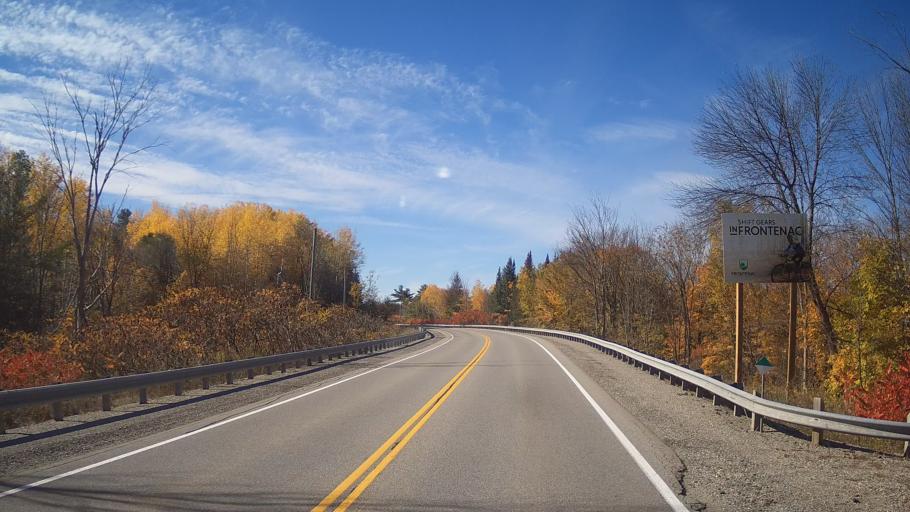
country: CA
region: Ontario
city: Perth
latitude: 44.8203
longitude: -76.6124
